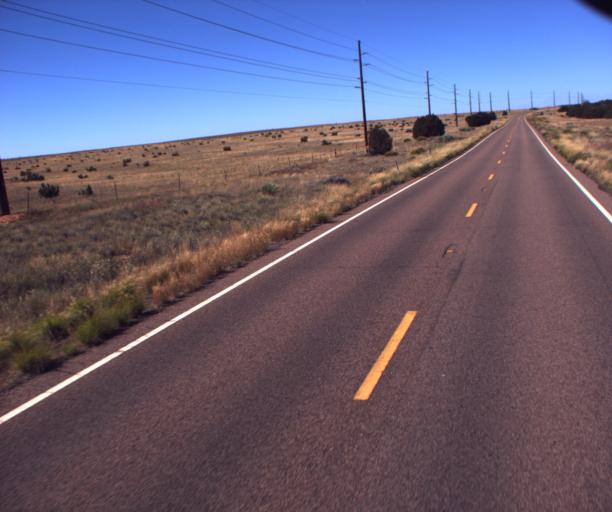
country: US
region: Arizona
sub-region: Navajo County
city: Taylor
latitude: 34.4824
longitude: -110.2966
